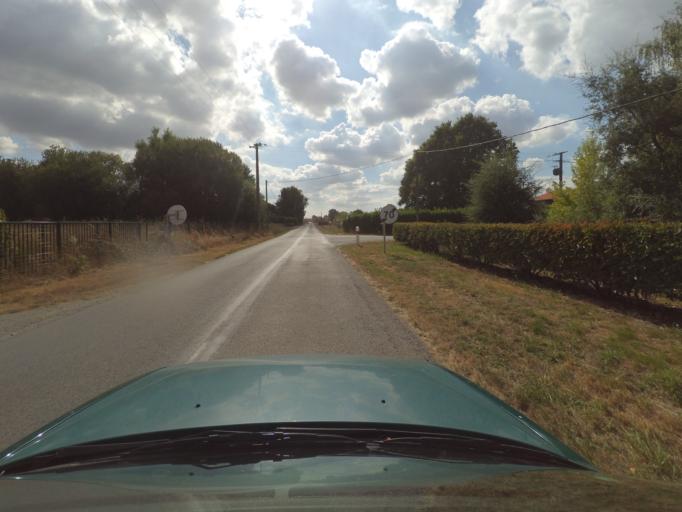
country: FR
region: Pays de la Loire
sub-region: Departement de la Loire-Atlantique
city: La Planche
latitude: 47.0109
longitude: -1.4463
